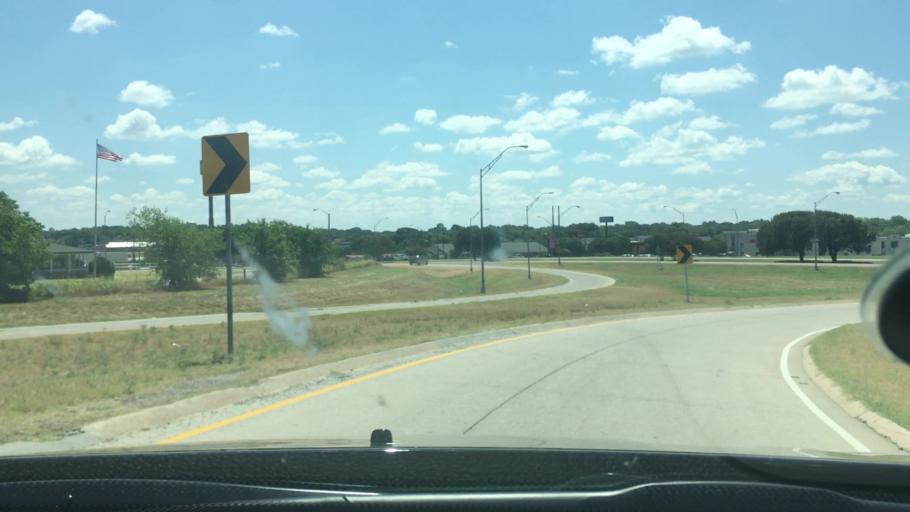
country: US
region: Oklahoma
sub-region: Carter County
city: Ardmore
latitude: 34.1741
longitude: -97.1667
